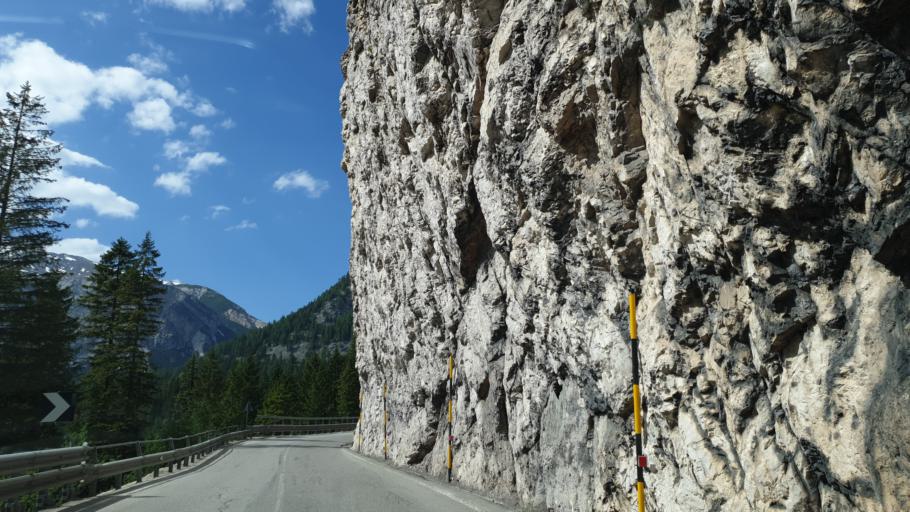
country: IT
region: Veneto
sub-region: Provincia di Belluno
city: Cortina d'Ampezzo
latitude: 46.5965
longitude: 12.1099
